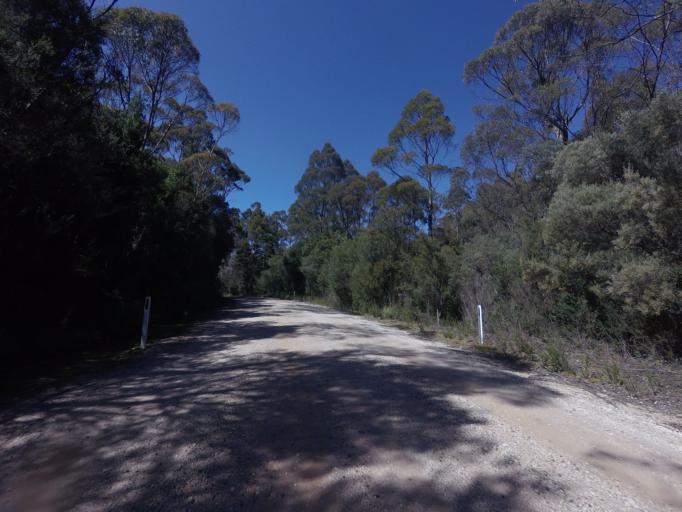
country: AU
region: Tasmania
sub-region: Huon Valley
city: Geeveston
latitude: -42.9849
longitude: 146.3639
